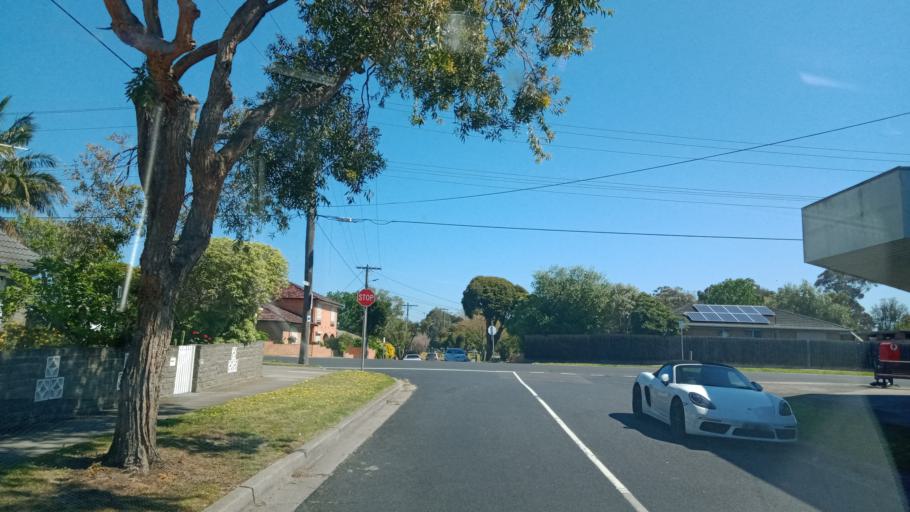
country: AU
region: Victoria
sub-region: Monash
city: Oakleigh South
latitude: -37.9324
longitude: 145.0827
